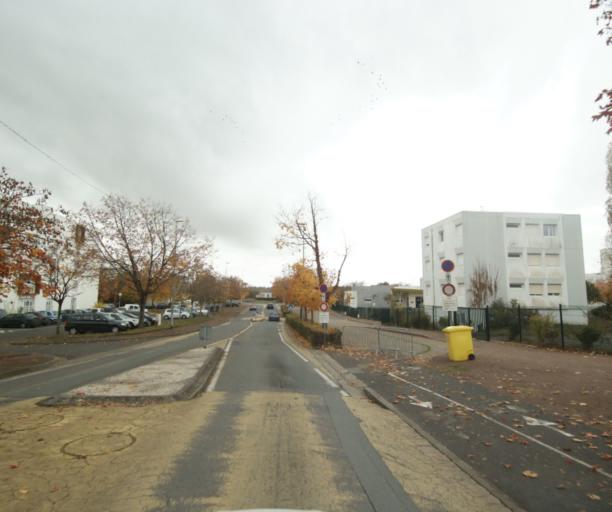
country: FR
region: Poitou-Charentes
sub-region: Departement de la Charente-Maritime
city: Saintes
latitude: 45.7360
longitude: -0.6516
